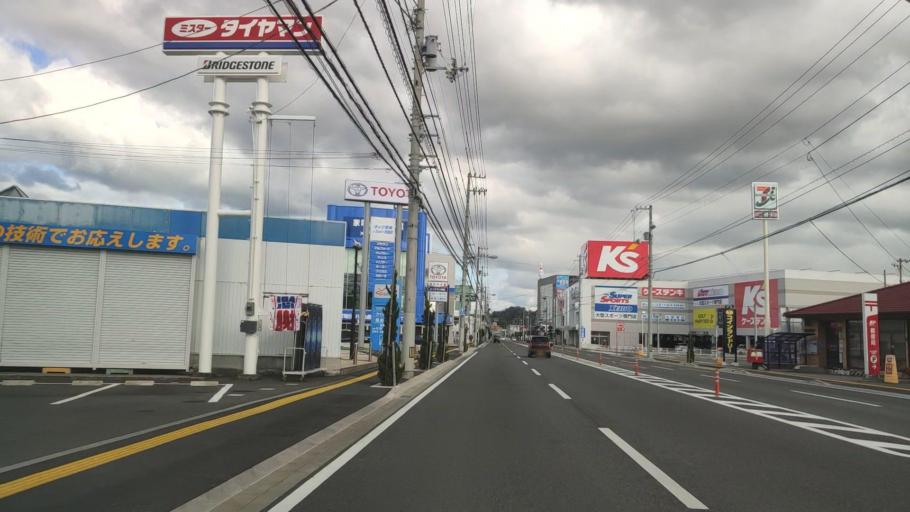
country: JP
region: Ehime
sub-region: Shikoku-chuo Shi
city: Matsuyama
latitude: 33.8634
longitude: 132.7501
